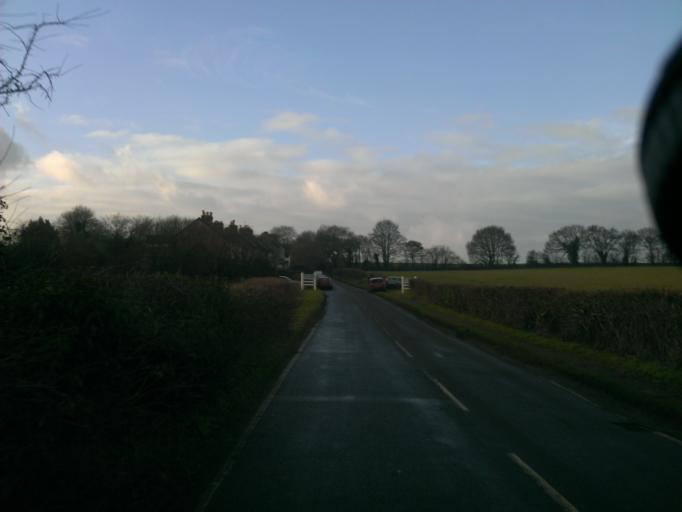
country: GB
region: England
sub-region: Suffolk
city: Sudbury
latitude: 52.0350
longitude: 0.7102
